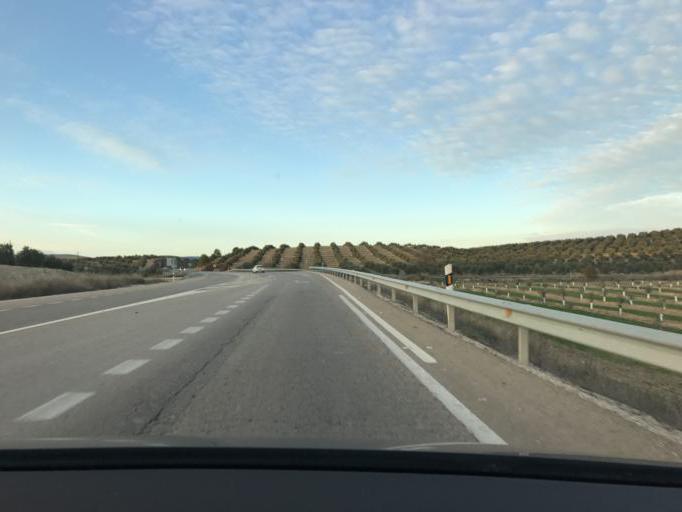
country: ES
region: Andalusia
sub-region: Provincia de Jaen
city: Jodar
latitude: 37.9270
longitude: -3.3541
